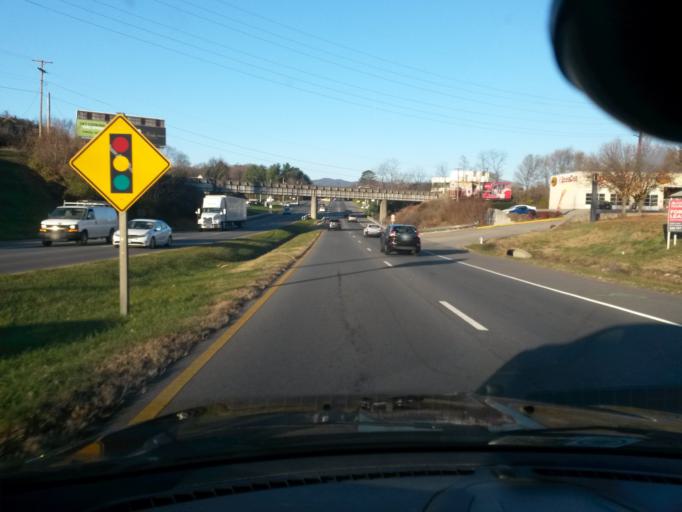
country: US
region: Virginia
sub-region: Roanoke County
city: Cave Spring
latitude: 37.2241
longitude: -79.9885
